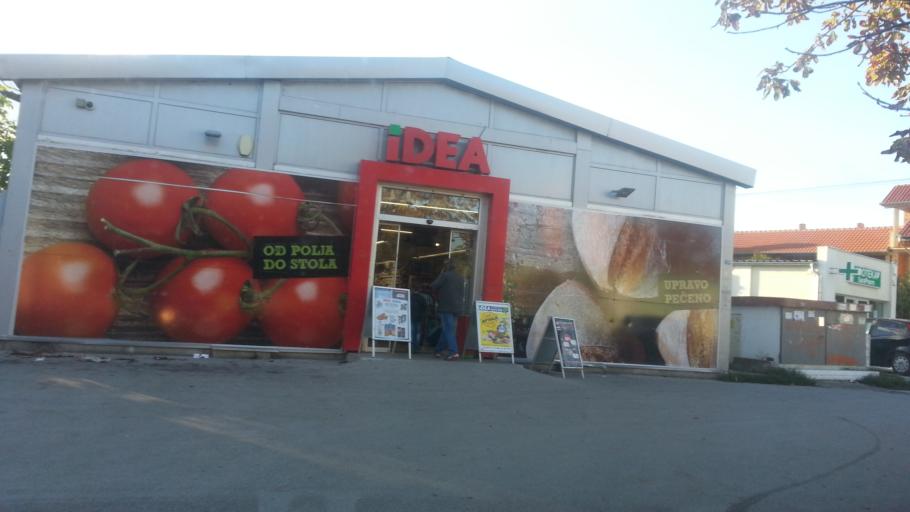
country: RS
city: Novi Banovci
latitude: 44.9121
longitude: 20.2812
